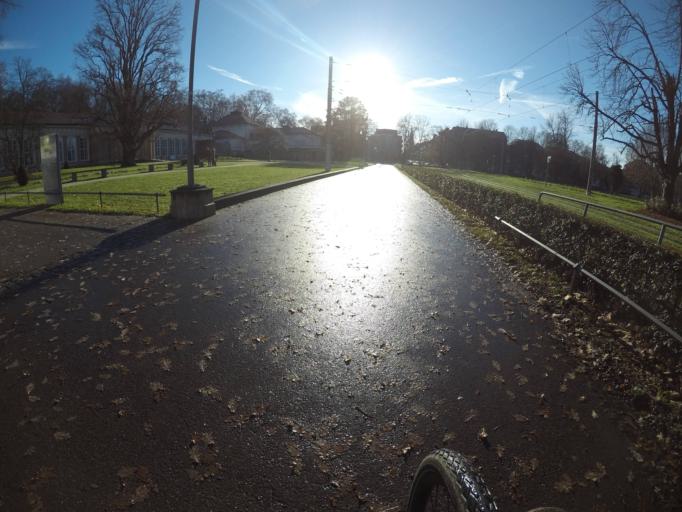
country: DE
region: Baden-Wuerttemberg
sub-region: Regierungsbezirk Stuttgart
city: Stuttgart-Ost
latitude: 48.8089
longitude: 9.2225
